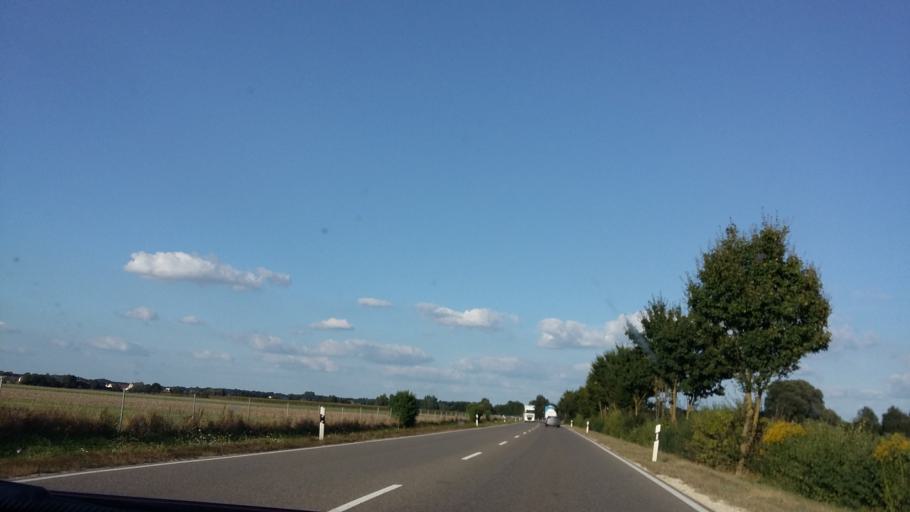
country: DE
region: Bavaria
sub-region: Swabia
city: Holzheim
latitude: 48.3963
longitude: 10.0632
